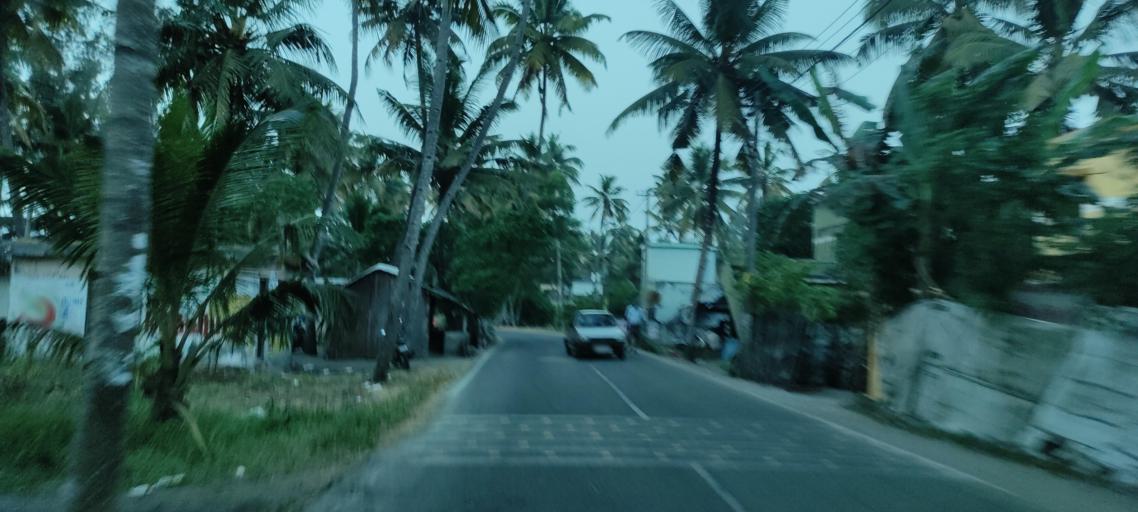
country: IN
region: Kerala
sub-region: Alappuzha
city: Kayankulam
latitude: 9.1296
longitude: 76.4662
